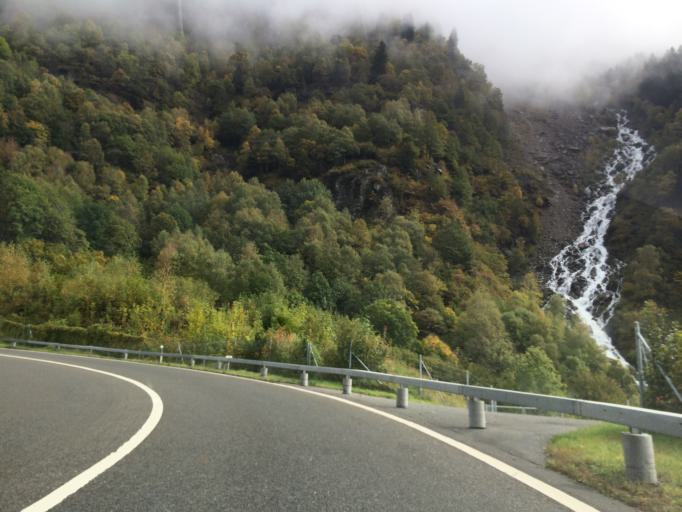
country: CH
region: Grisons
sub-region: Moesa District
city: Mesocco
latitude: 46.4078
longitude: 9.2385
